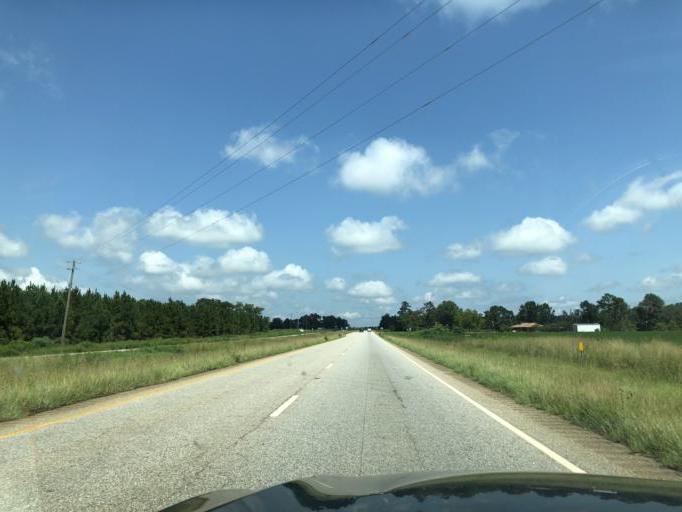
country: US
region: Alabama
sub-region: Henry County
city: Abbeville
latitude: 31.6140
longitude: -85.2772
